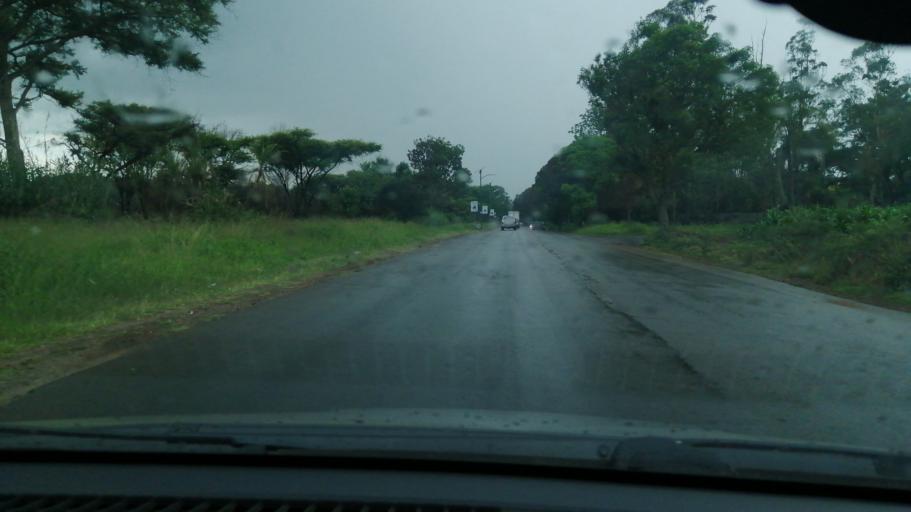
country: ZW
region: Harare
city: Harare
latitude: -17.7894
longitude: 31.0541
